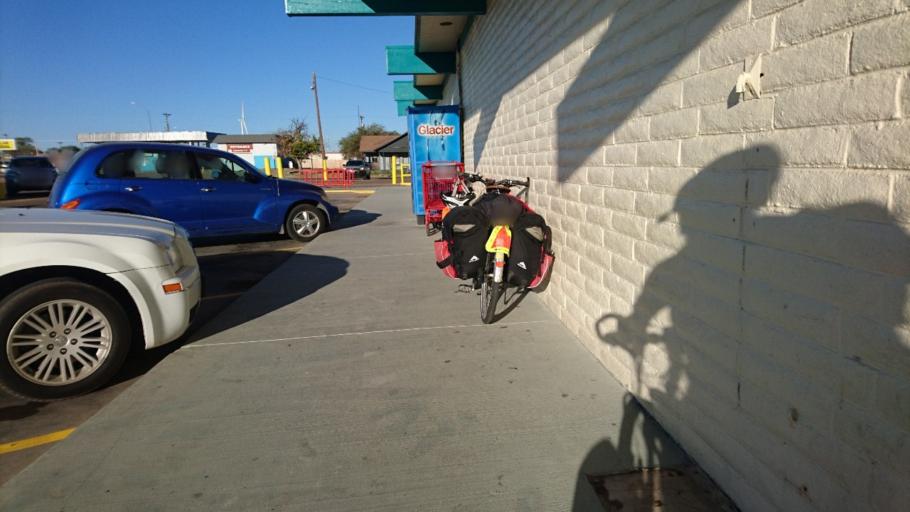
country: US
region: New Mexico
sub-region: Quay County
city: Tucumcari
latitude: 35.1724
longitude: -103.7268
